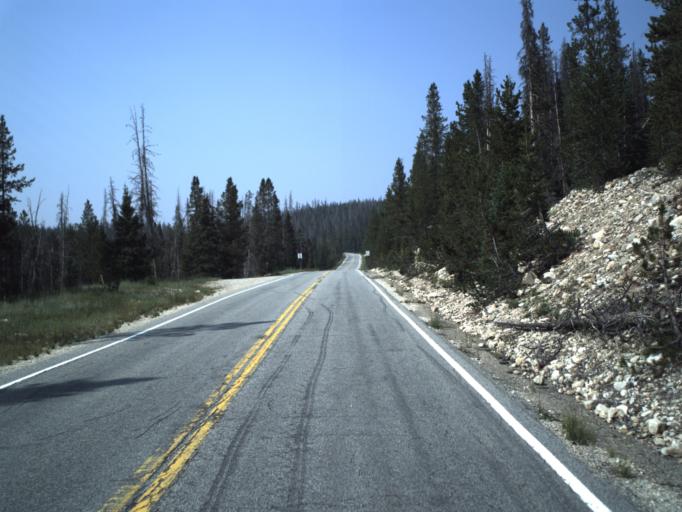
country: US
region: Utah
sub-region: Summit County
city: Kamas
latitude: 40.6509
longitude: -110.9451
